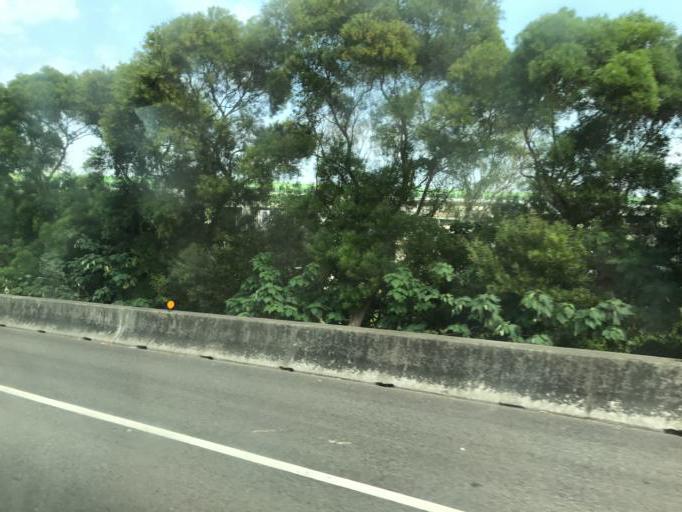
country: TW
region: Taiwan
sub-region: Hsinchu
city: Zhubei
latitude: 24.8092
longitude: 121.0107
